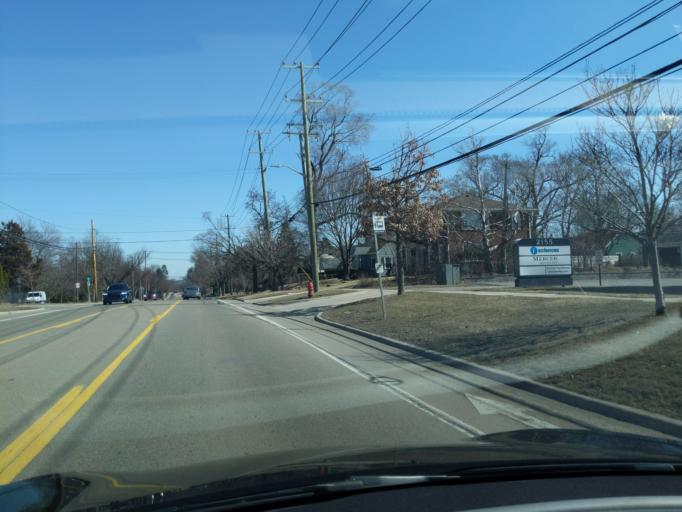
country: US
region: Michigan
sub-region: Washtenaw County
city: Ann Arbor
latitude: 42.2806
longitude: -83.7769
